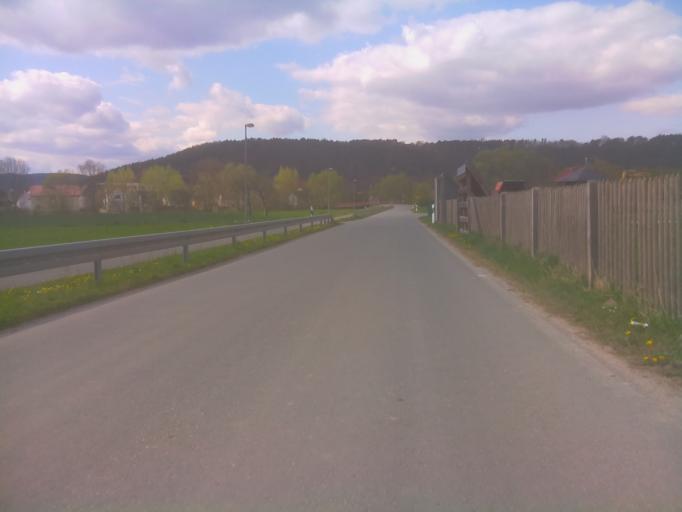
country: DE
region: Thuringia
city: Schops
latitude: 50.8329
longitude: 11.6016
